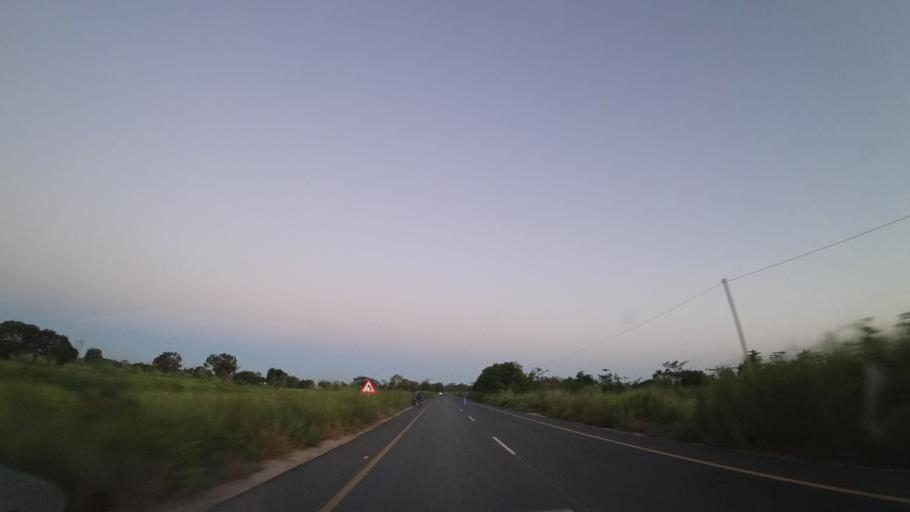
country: MZ
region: Sofala
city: Dondo
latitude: -19.5529
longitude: 34.6507
